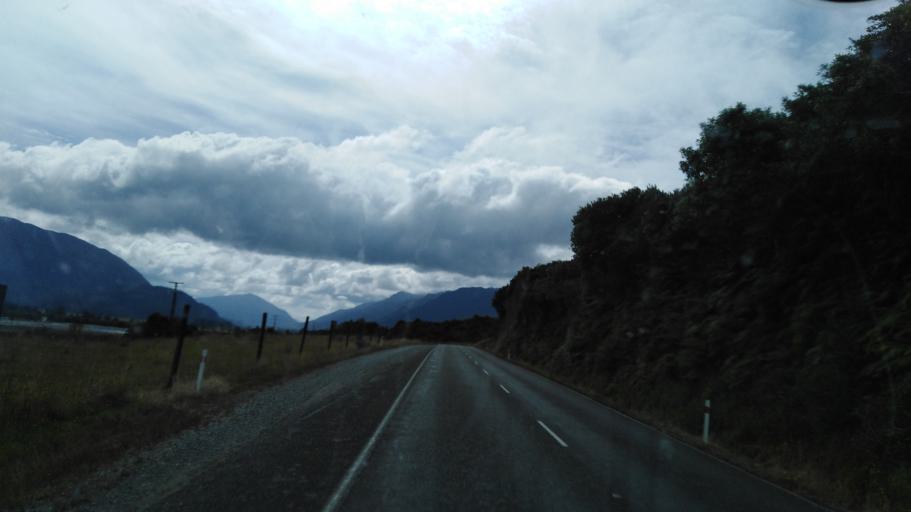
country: NZ
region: West Coast
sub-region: Grey District
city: Greymouth
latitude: -42.7365
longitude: 171.4351
